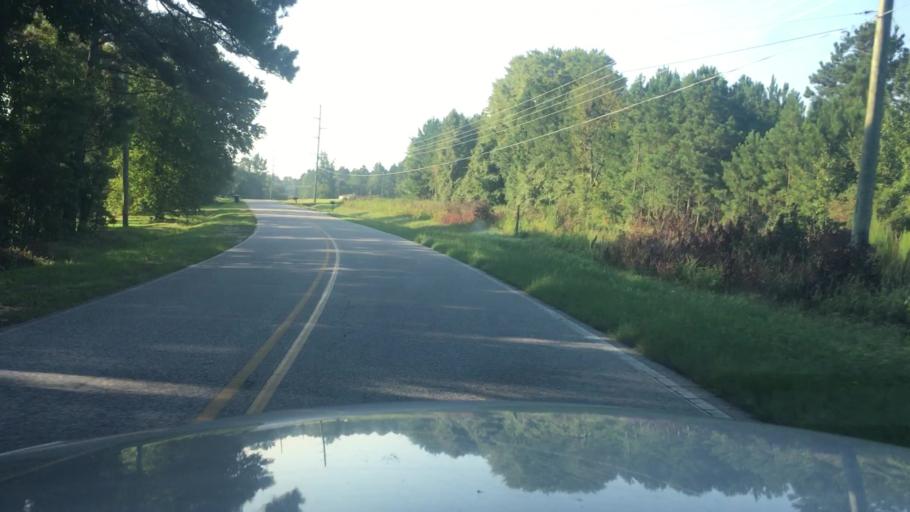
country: US
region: North Carolina
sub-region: Cumberland County
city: Spring Lake
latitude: 35.2101
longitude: -78.8950
